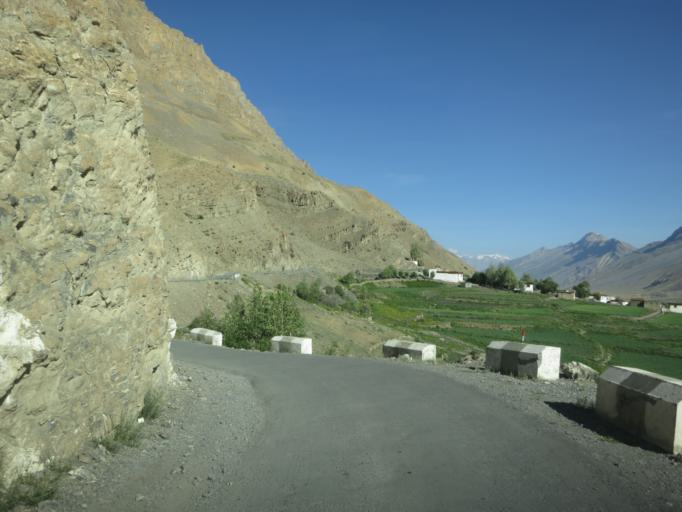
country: IN
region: Himachal Pradesh
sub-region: Shimla
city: Sarahan
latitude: 32.2949
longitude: 78.0102
